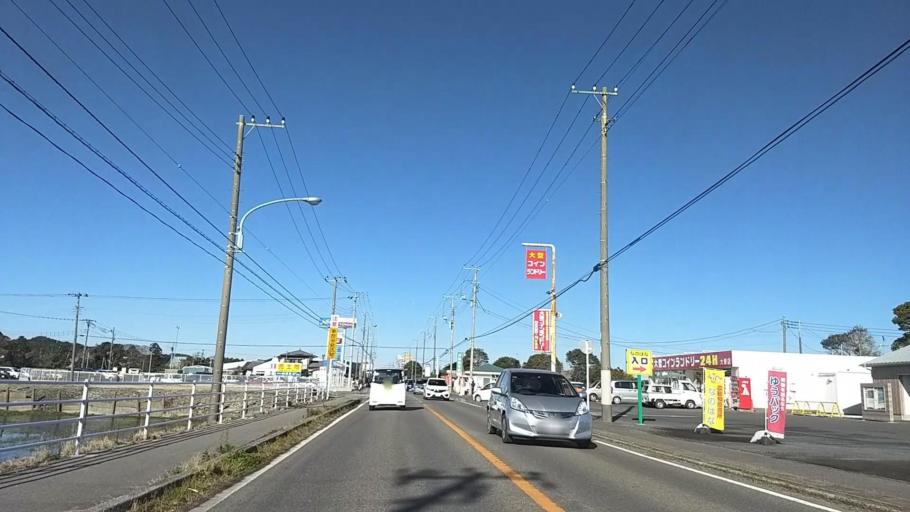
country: JP
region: Chiba
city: Ohara
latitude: 35.2662
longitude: 140.3939
